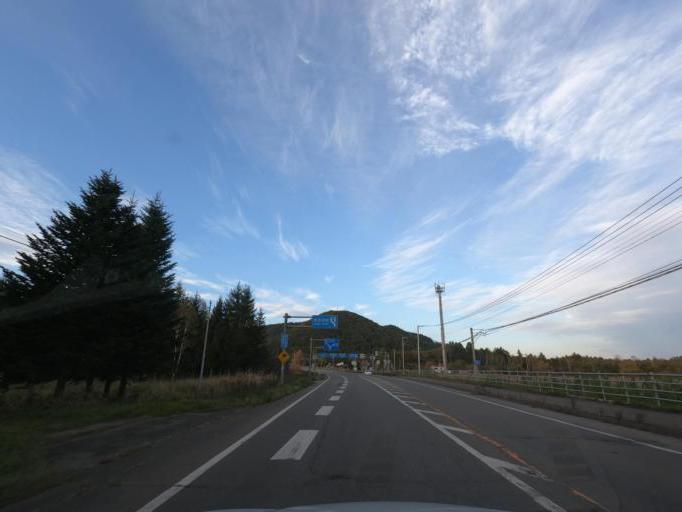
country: JP
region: Hokkaido
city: Obihiro
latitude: 42.5730
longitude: 143.3085
